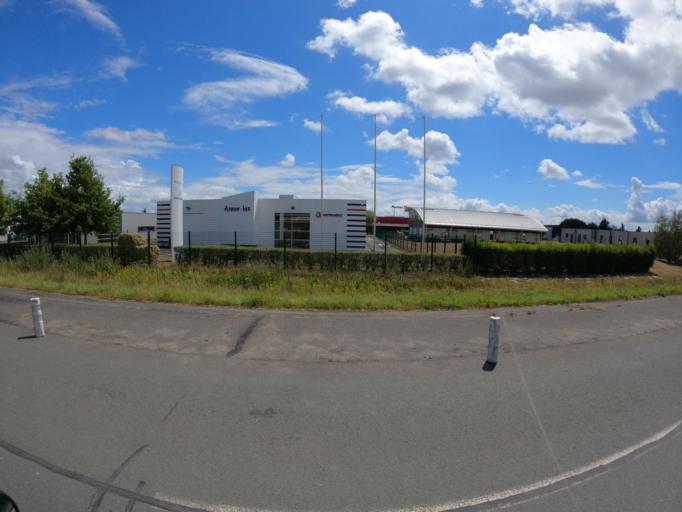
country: FR
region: Pays de la Loire
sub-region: Departement de Maine-et-Loire
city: Avrille
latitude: 47.5152
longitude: -0.6161
